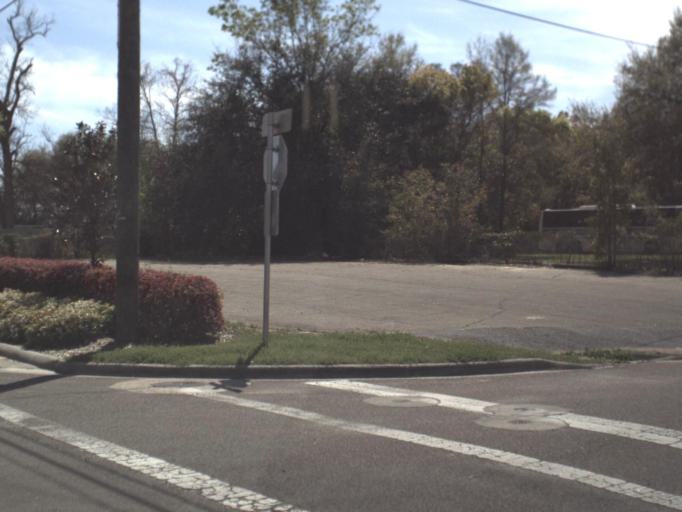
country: US
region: Florida
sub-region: Bay County
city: Panama City
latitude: 30.1670
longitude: -85.6504
